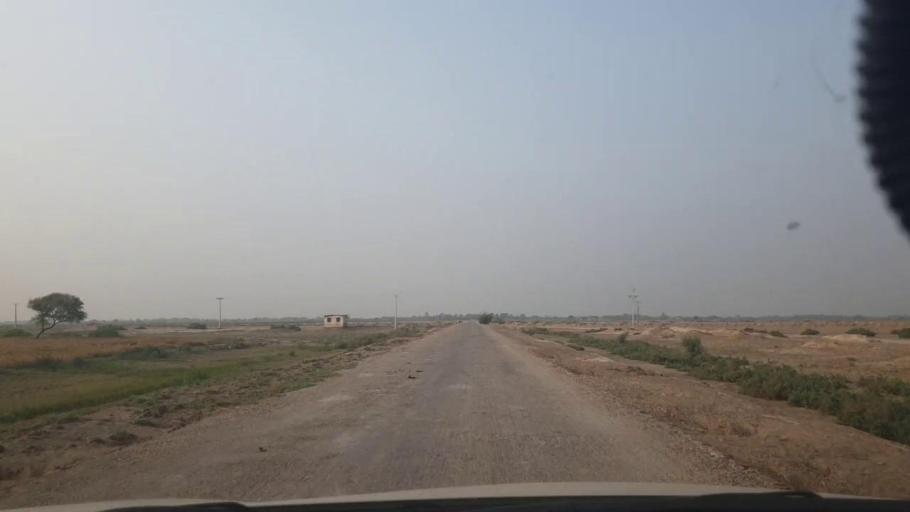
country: PK
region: Sindh
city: Bulri
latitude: 24.8154
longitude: 68.4066
